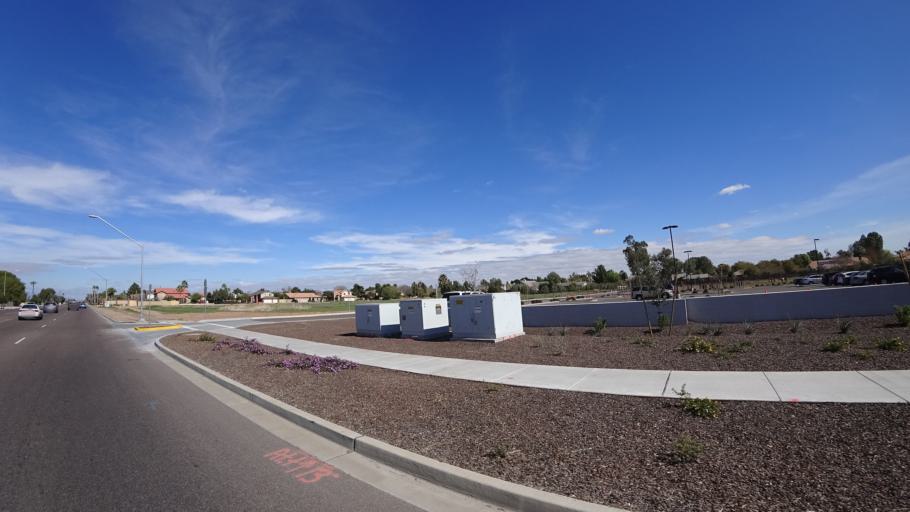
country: US
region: Arizona
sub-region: Maricopa County
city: Peoria
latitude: 33.6129
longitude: -112.2025
